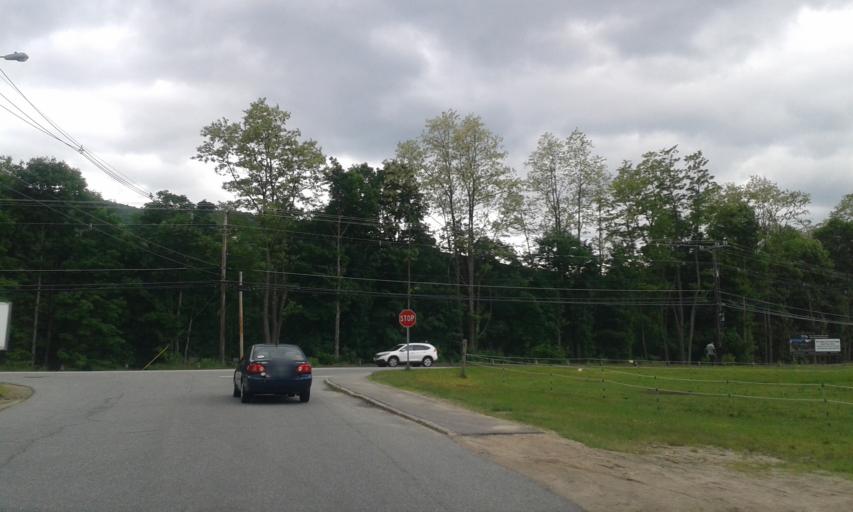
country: US
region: New Hampshire
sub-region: Grafton County
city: Woodstock
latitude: 44.0484
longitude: -71.6641
